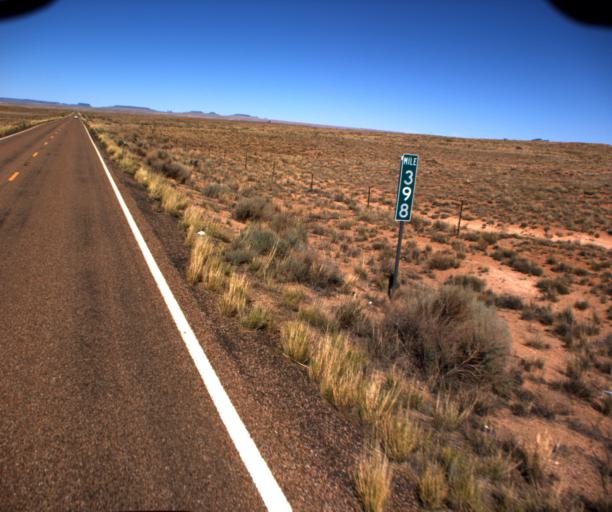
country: US
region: Arizona
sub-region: Navajo County
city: Holbrook
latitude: 35.0138
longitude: -110.0900
